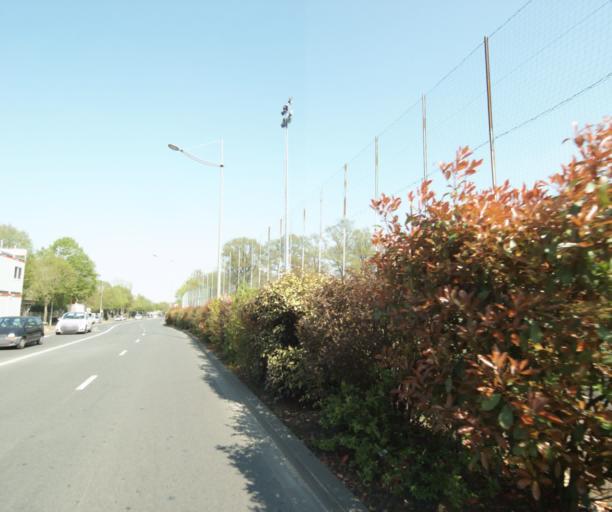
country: FR
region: Ile-de-France
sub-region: Departement des Hauts-de-Seine
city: Sevres
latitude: 48.8097
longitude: 2.2069
